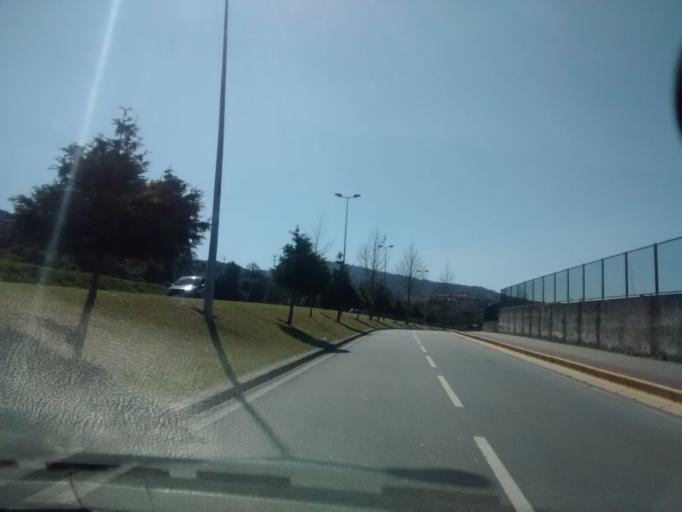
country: PT
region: Braga
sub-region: Braga
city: Braga
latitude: 41.5498
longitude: -8.3957
